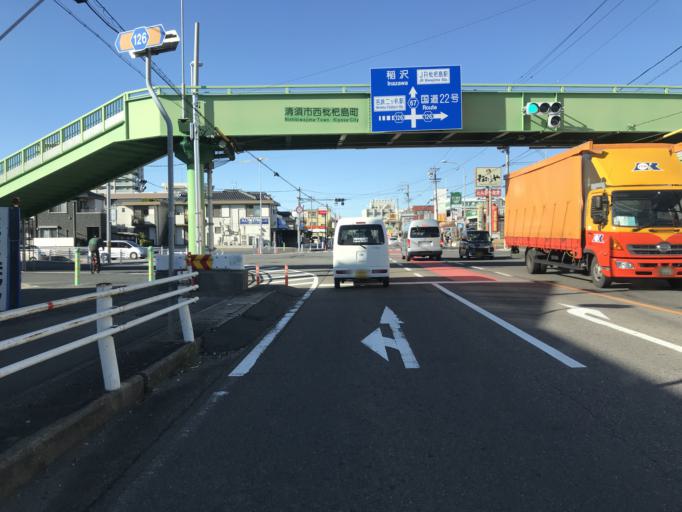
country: JP
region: Aichi
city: Nagoya-shi
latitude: 35.1981
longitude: 136.8643
